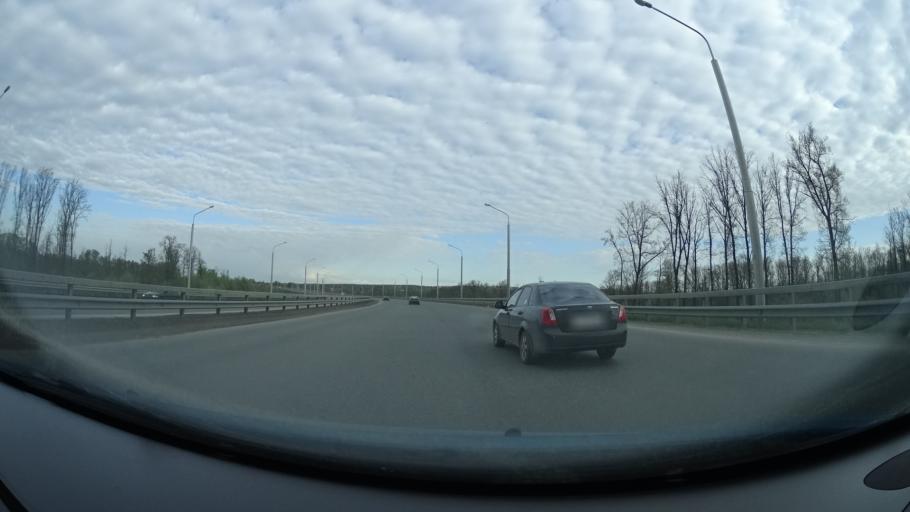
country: RU
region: Bashkortostan
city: Mikhaylovka
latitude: 54.7942
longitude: 55.9034
